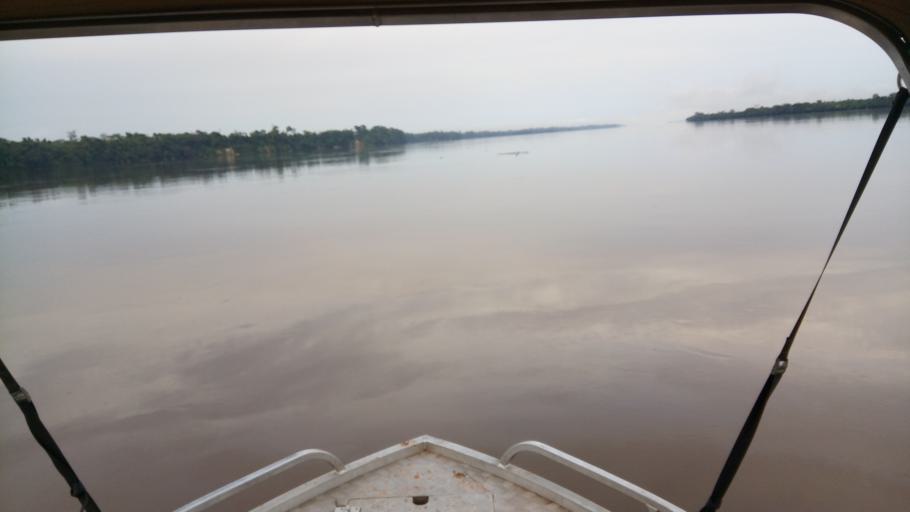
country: CD
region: Eastern Province
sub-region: Sous-Region de la Tshopo
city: Yangambi
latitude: 0.5736
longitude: 24.7707
